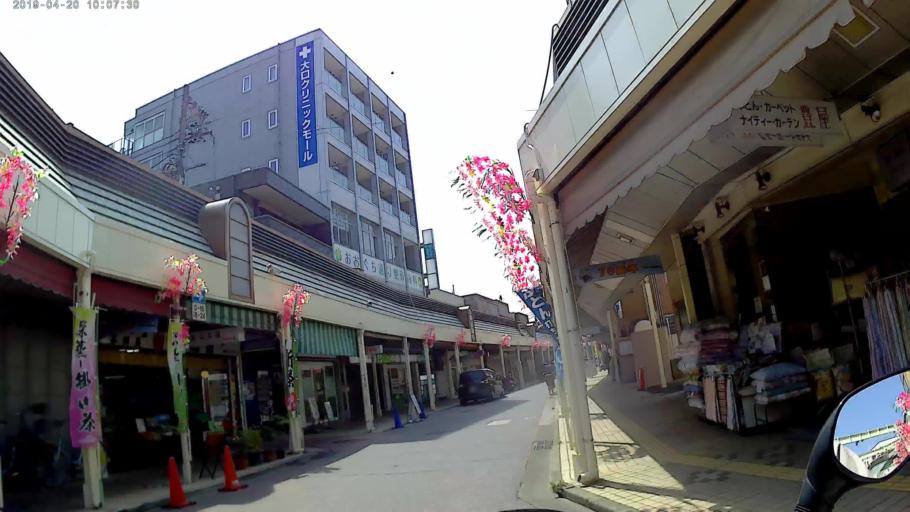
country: JP
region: Kanagawa
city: Yokohama
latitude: 35.4886
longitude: 139.6455
